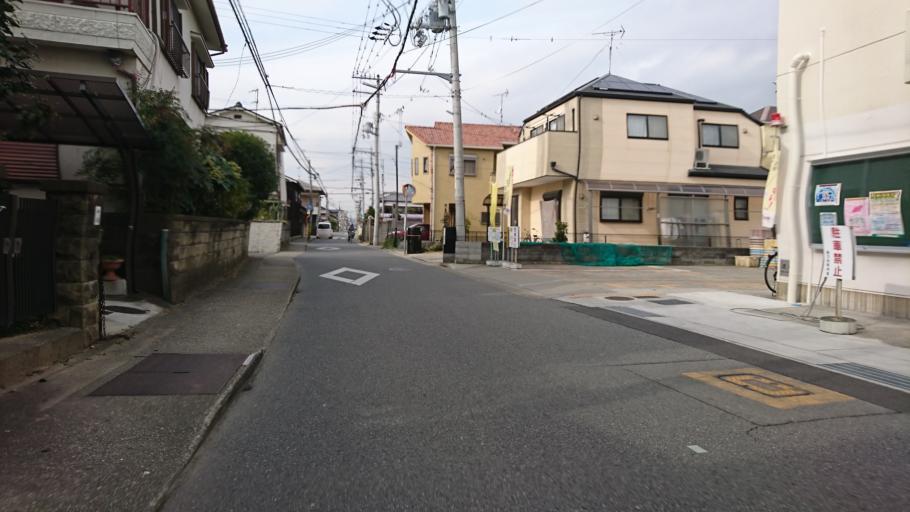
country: JP
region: Hyogo
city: Kakogawacho-honmachi
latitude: 34.7676
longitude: 134.8540
